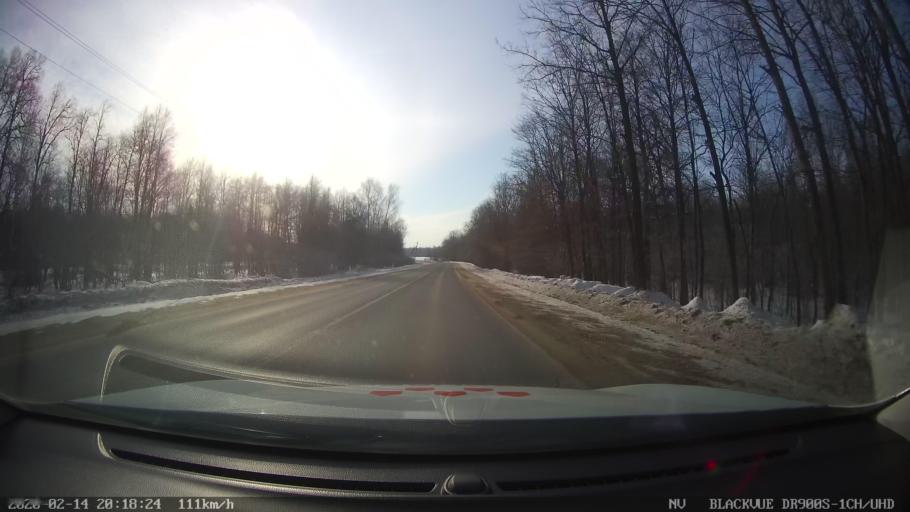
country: RU
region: Tatarstan
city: Verkhniy Uslon
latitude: 55.5863
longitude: 48.8870
